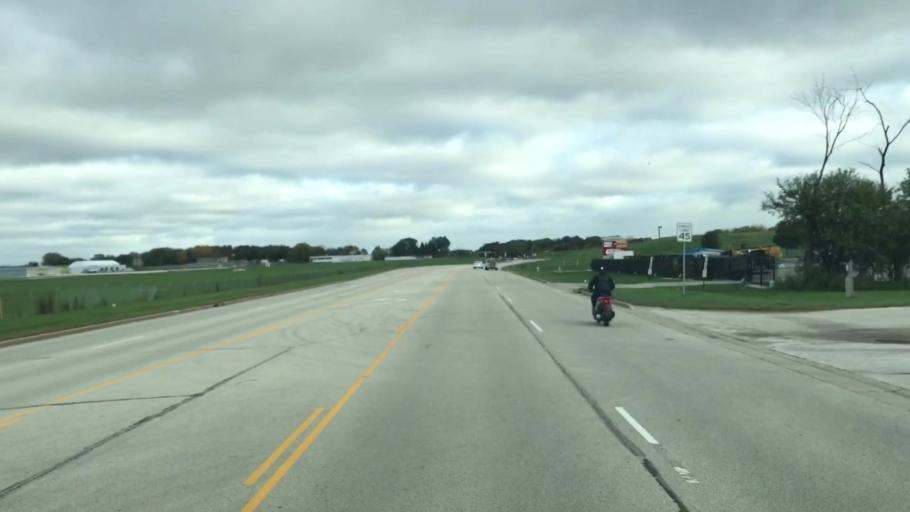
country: US
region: Wisconsin
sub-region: Waukesha County
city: Waukesha
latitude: 43.0363
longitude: -88.2257
